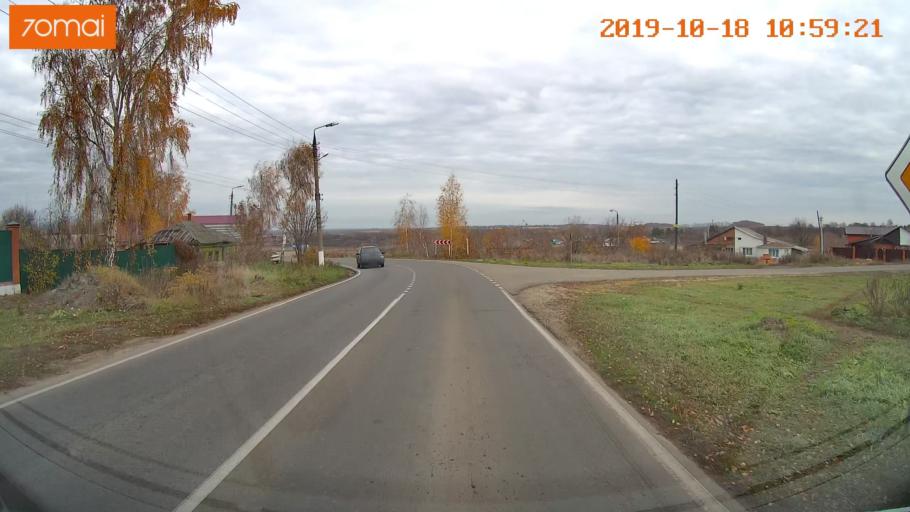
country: RU
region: Tula
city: Yepifan'
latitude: 53.8295
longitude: 38.5569
